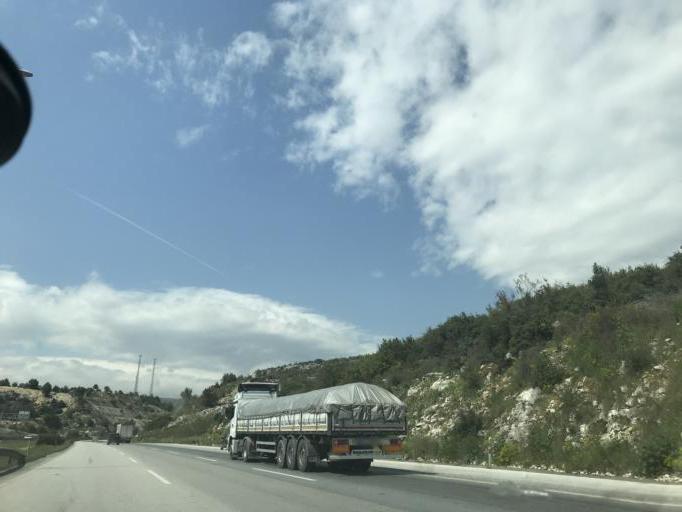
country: TR
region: Mersin
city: Tarsus
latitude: 37.1495
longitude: 34.8408
